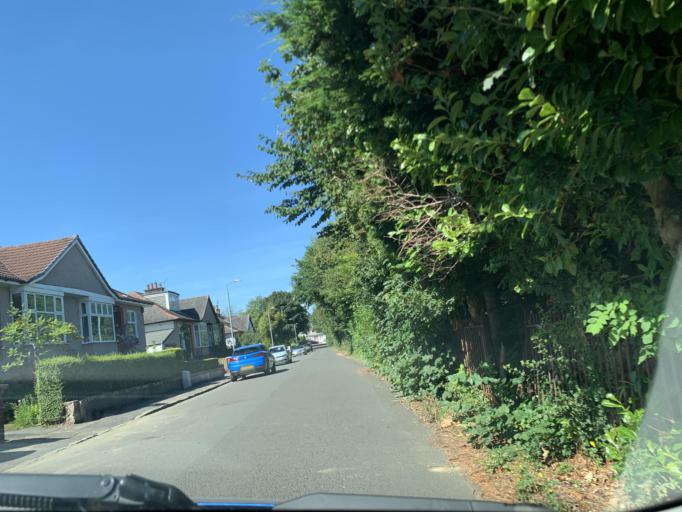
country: GB
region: Scotland
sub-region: East Renfrewshire
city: Giffnock
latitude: 55.8122
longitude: -4.2875
